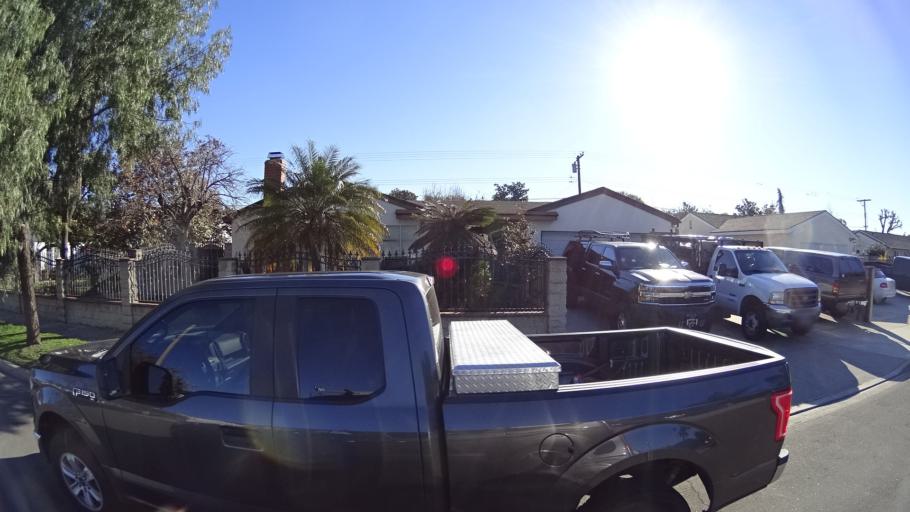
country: US
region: California
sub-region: Orange County
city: Stanton
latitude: 33.8129
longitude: -118.0134
